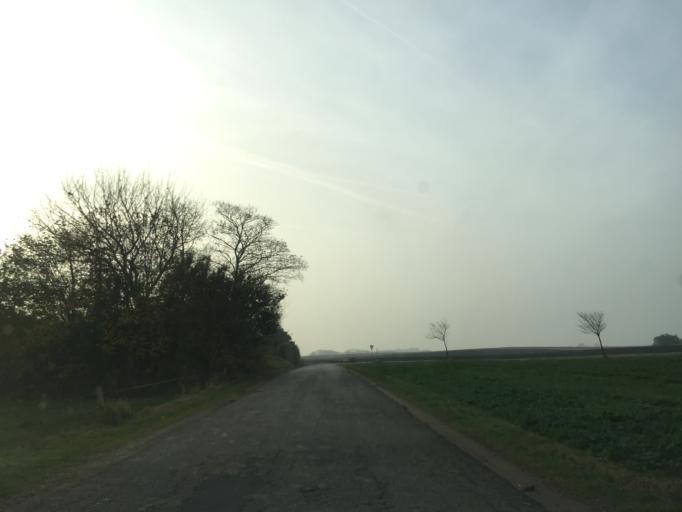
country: DK
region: Central Jutland
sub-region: Silkeborg Kommune
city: Svejbaek
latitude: 56.2283
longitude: 9.6452
